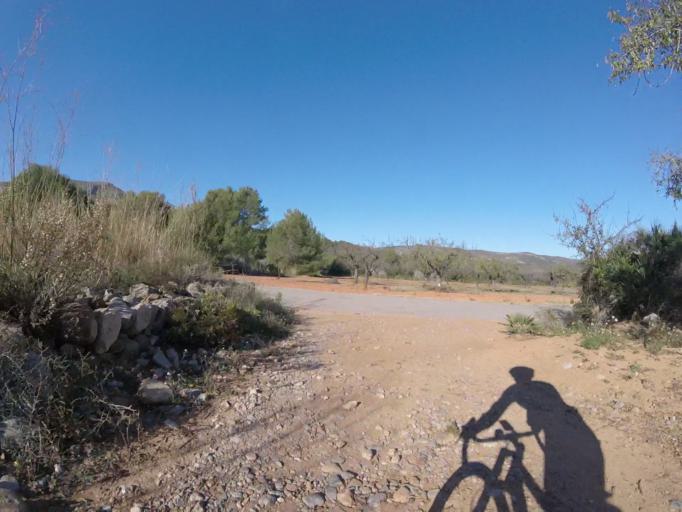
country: ES
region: Valencia
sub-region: Provincia de Castello
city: Orpesa/Oropesa del Mar
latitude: 40.1238
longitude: 0.1127
